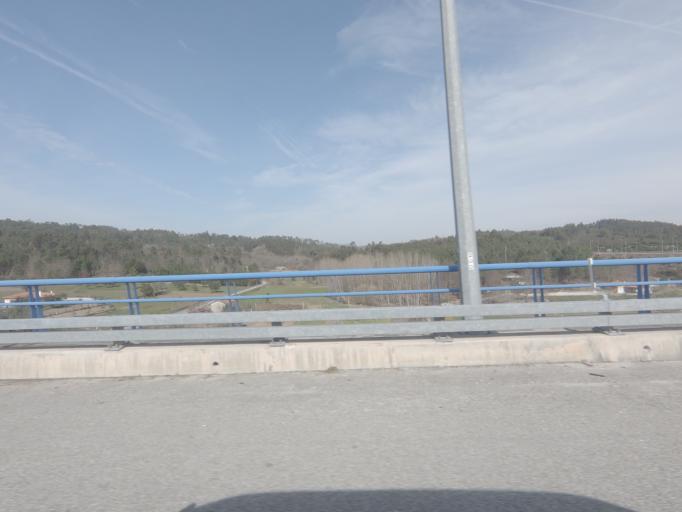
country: PT
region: Viseu
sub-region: Viseu
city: Viseu
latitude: 40.6262
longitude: -7.9645
